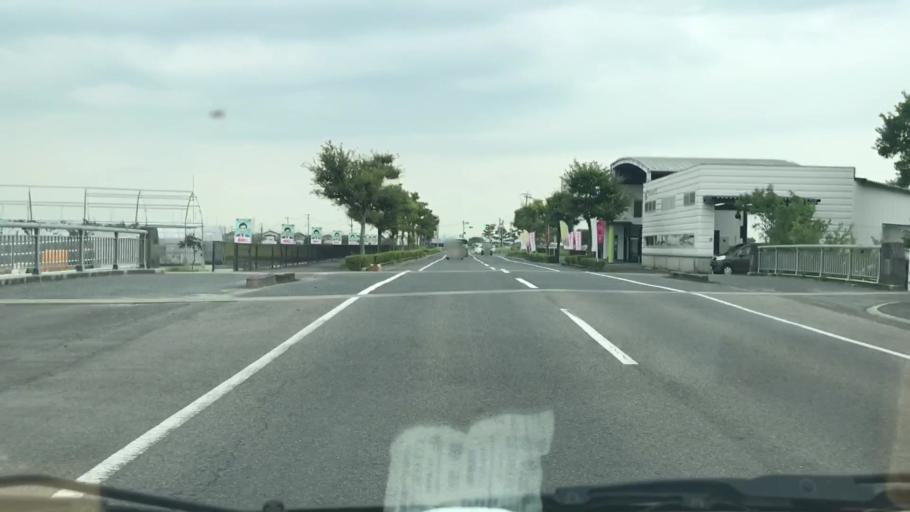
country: JP
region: Saga Prefecture
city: Saga-shi
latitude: 33.2343
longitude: 130.3029
